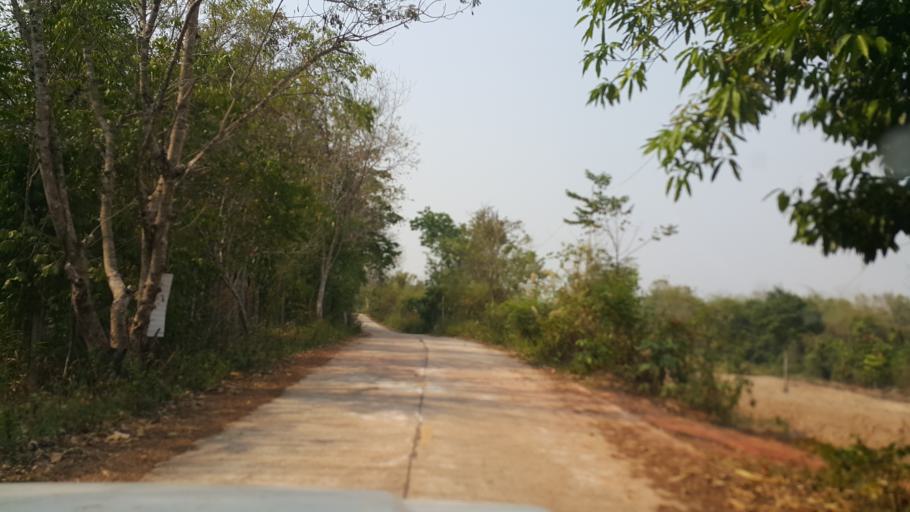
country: TH
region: Nakhon Phanom
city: Ban Phaeng
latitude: 17.9817
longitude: 104.1471
